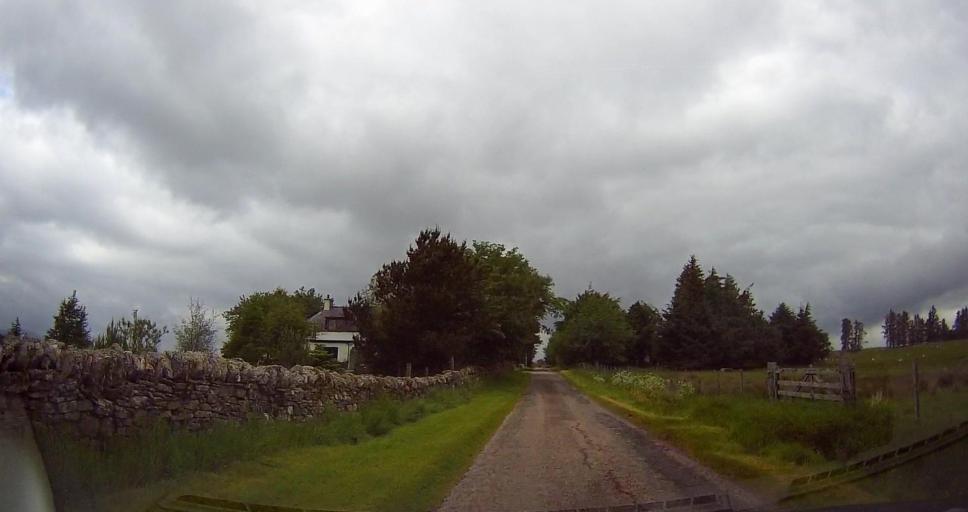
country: GB
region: Scotland
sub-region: Highland
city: Alness
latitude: 58.0749
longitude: -4.4402
